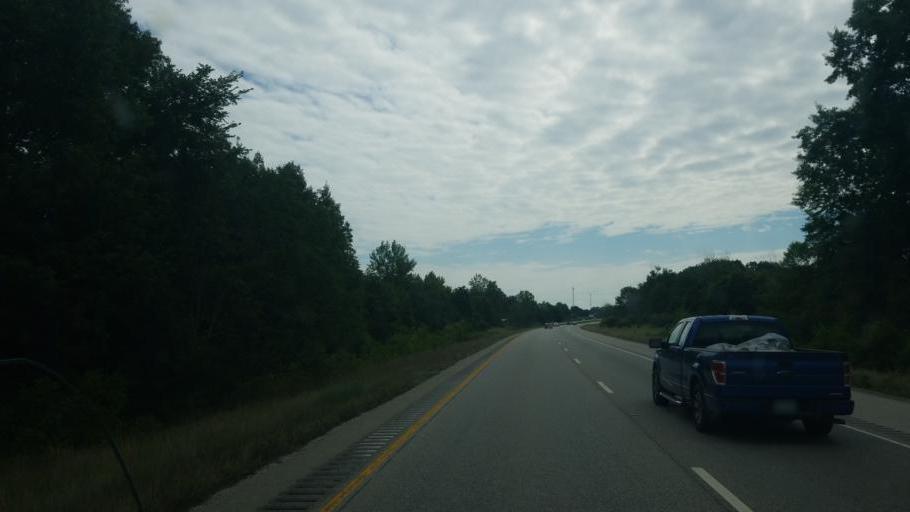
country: US
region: Indiana
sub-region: Vigo County
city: Seelyville
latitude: 39.4451
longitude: -87.2542
